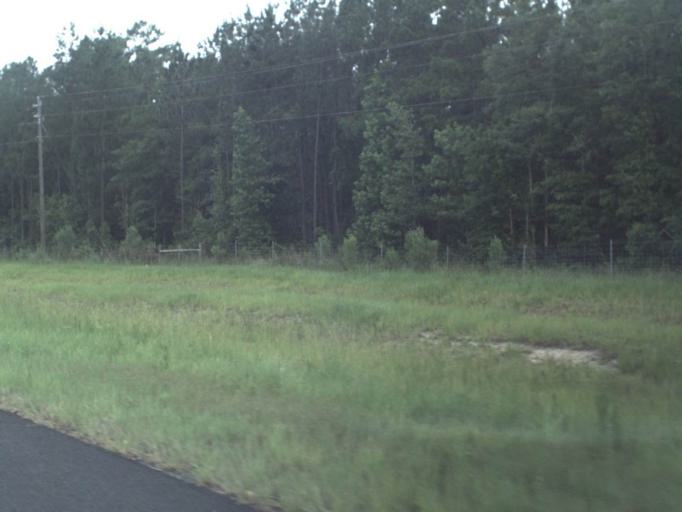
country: US
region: Florida
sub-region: Nassau County
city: Callahan
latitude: 30.5423
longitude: -81.8506
